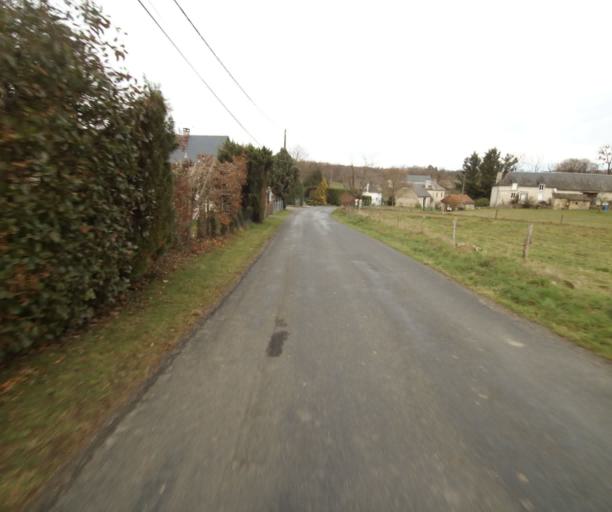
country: FR
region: Limousin
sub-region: Departement de la Correze
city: Chameyrat
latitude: 45.2455
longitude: 1.6852
